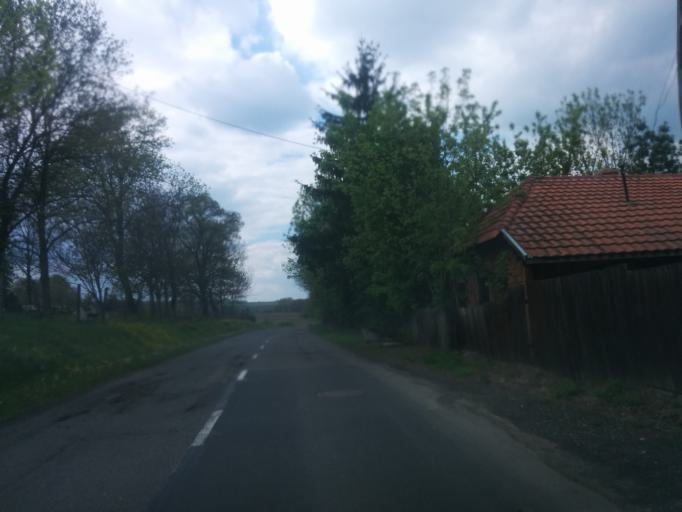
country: HU
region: Nograd
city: Palotas
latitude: 47.8254
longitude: 19.5803
